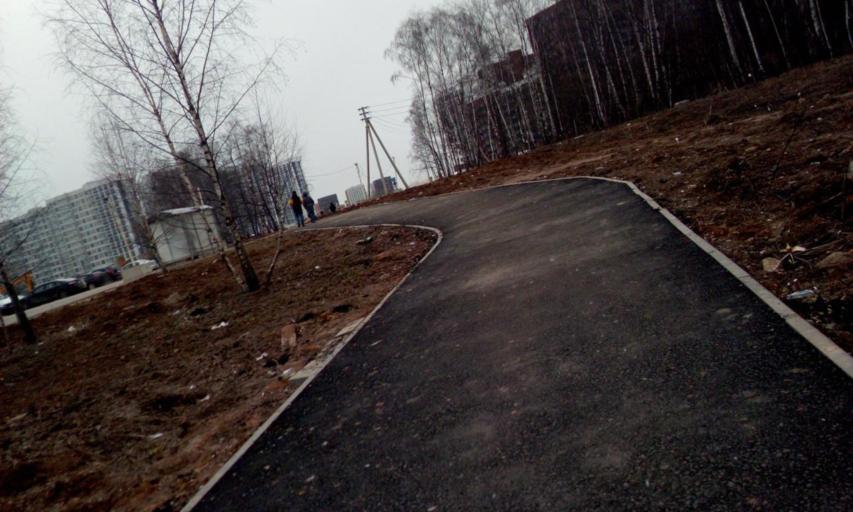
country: RU
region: Moskovskaya
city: Kommunarka
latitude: 55.5539
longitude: 37.5123
